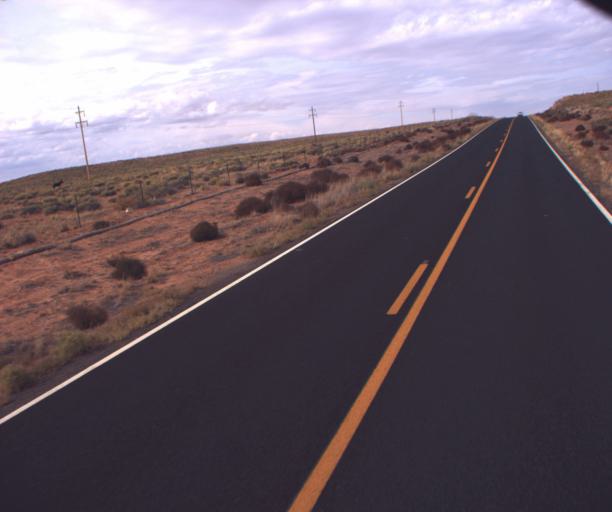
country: US
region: Arizona
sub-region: Apache County
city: Many Farms
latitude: 36.5965
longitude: -109.5664
